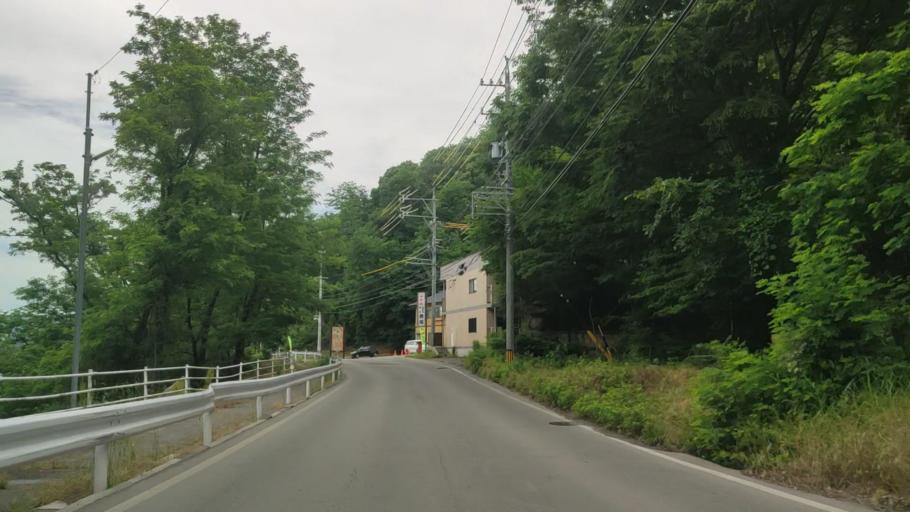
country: JP
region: Nagano
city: Kamimaruko
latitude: 36.3337
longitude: 138.3516
